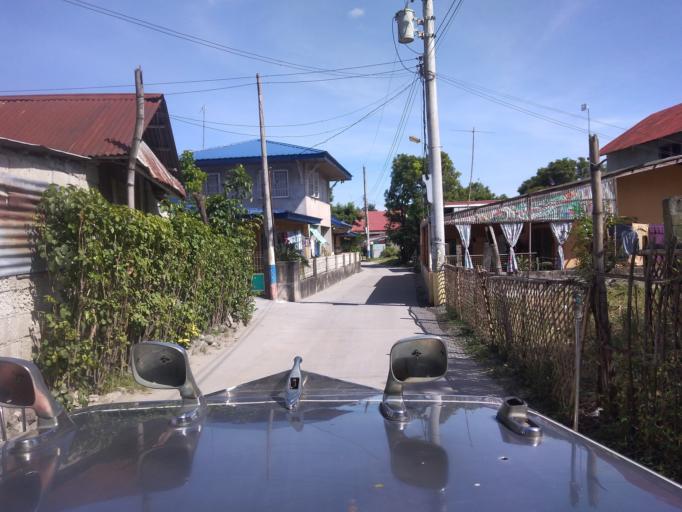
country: PH
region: Central Luzon
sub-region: Province of Pampanga
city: Magliman
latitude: 15.0267
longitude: 120.6558
